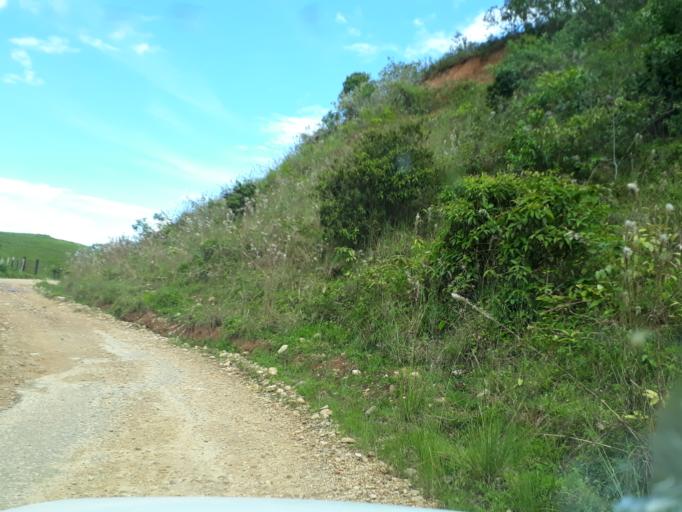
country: CO
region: Cundinamarca
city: Medina
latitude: 4.5940
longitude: -73.3109
